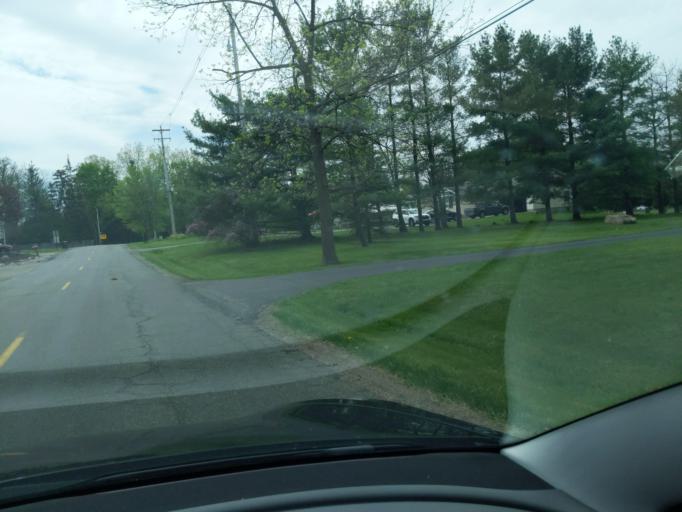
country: US
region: Michigan
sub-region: Ingham County
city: Holt
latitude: 42.6416
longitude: -84.5529
